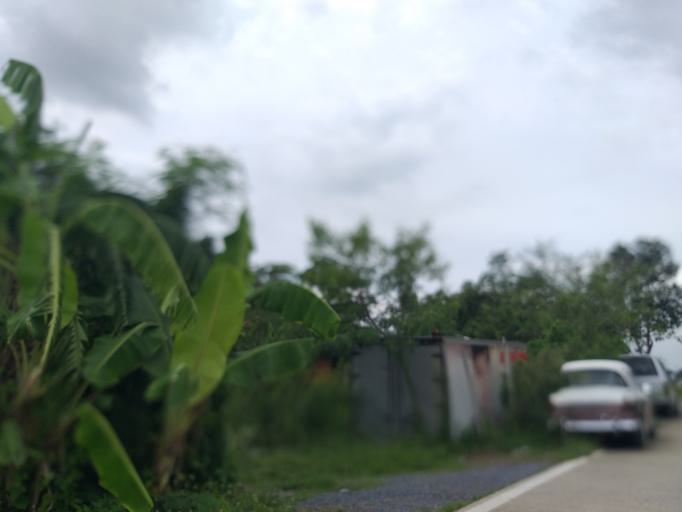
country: TH
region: Pathum Thani
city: Ban Lam Luk Ka
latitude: 13.9638
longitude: 100.8527
